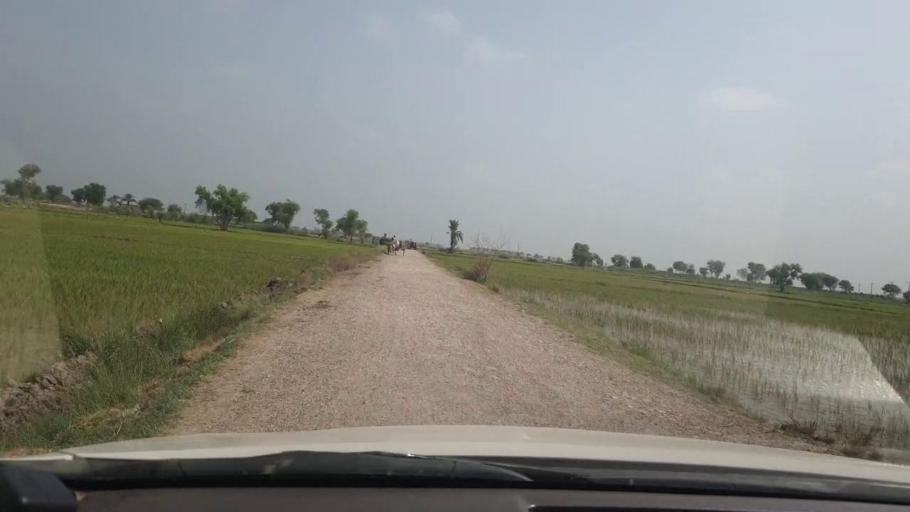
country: PK
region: Sindh
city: Shikarpur
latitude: 28.0127
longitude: 68.5941
